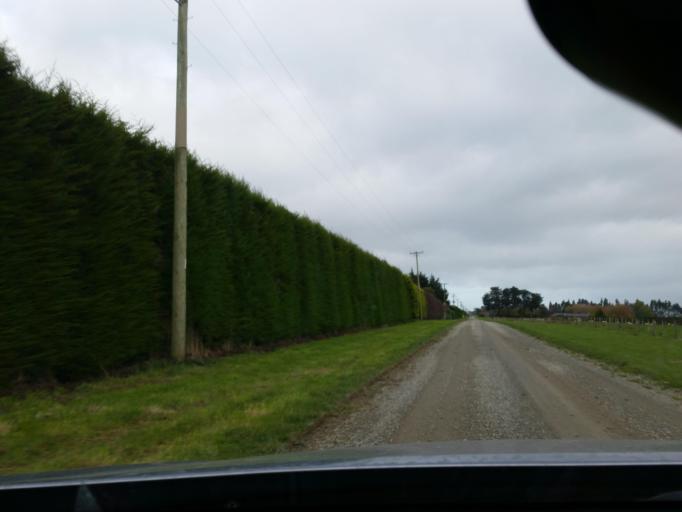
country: NZ
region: Southland
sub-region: Southland District
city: Winton
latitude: -46.2684
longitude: 168.3674
